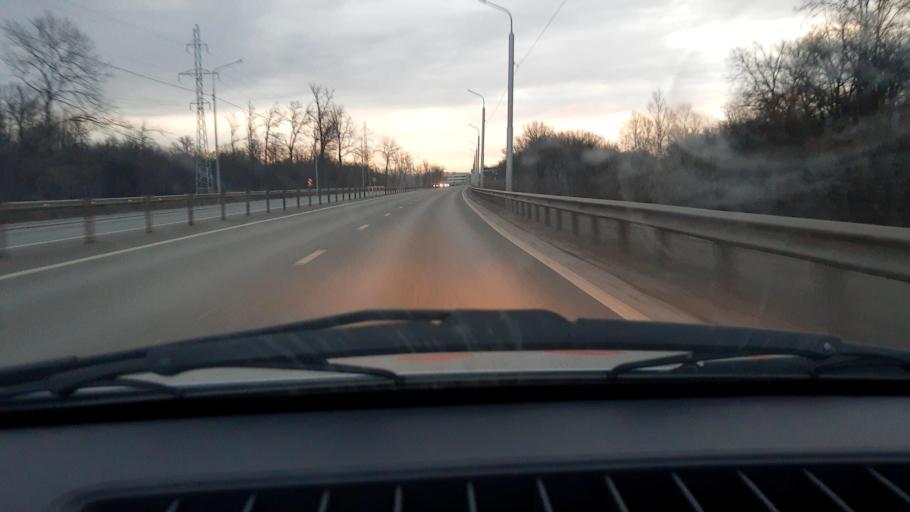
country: RU
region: Bashkortostan
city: Ufa
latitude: 54.6993
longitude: 55.8802
